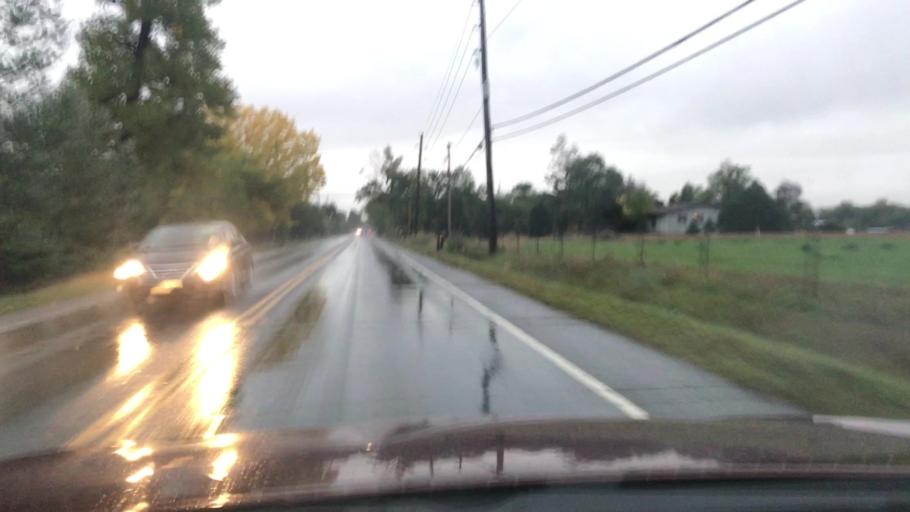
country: US
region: Colorado
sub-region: Boulder County
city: Gunbarrel
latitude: 40.0509
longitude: -105.1991
